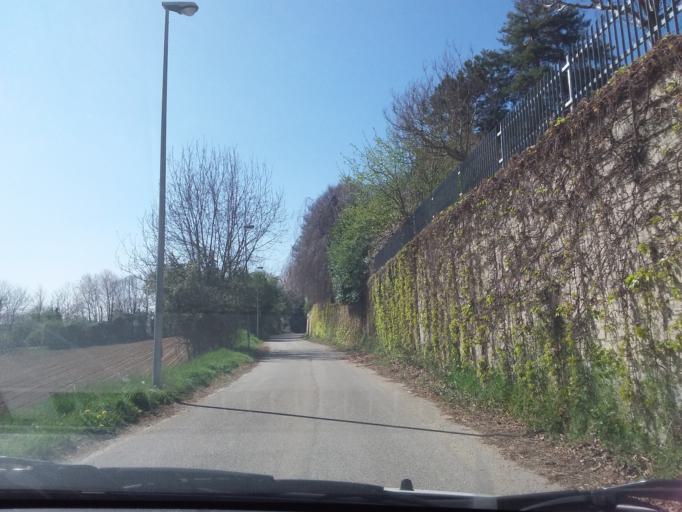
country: IT
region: Piedmont
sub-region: Provincia di Torino
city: Rivoli
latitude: 45.0643
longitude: 7.4979
